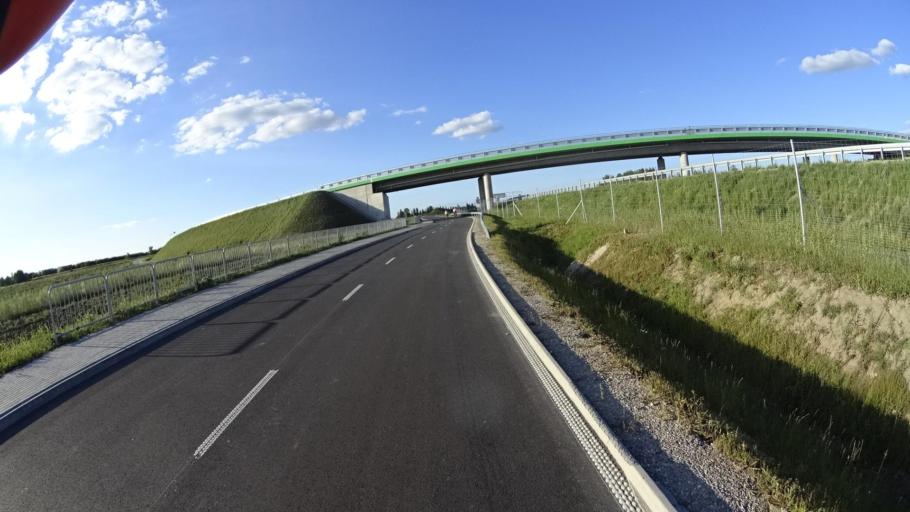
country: PL
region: Masovian Voivodeship
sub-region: Powiat piaseczynski
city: Lesznowola
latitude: 52.1017
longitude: 20.9693
